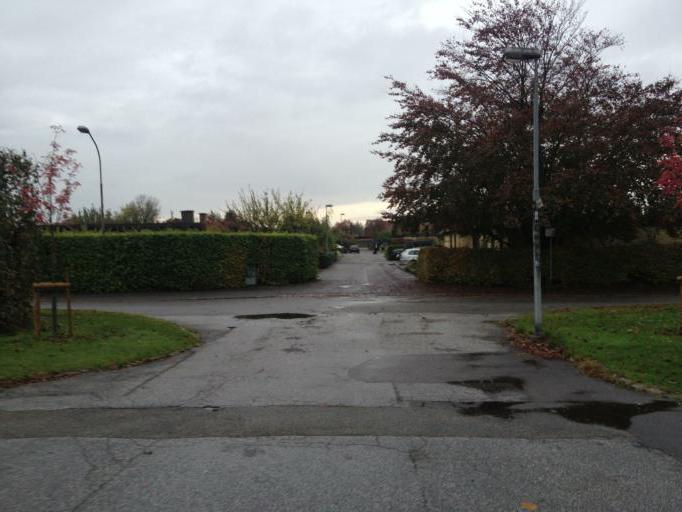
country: SE
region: Skane
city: Bjarred
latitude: 55.7241
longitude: 13.0231
